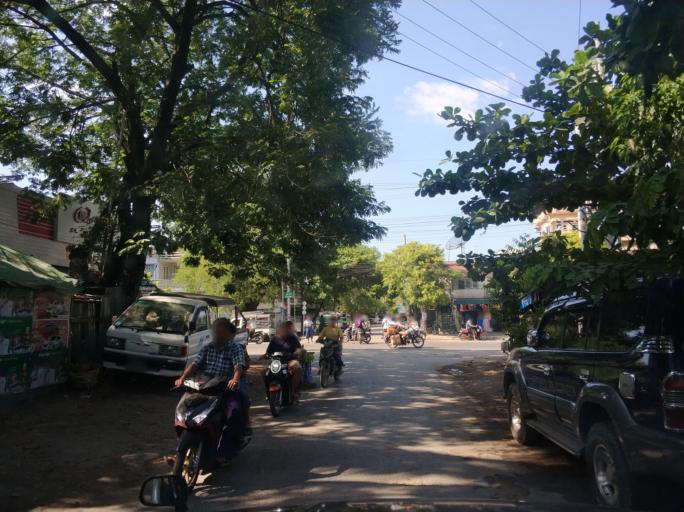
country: MM
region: Mandalay
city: Mandalay
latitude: 21.9704
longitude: 96.0687
